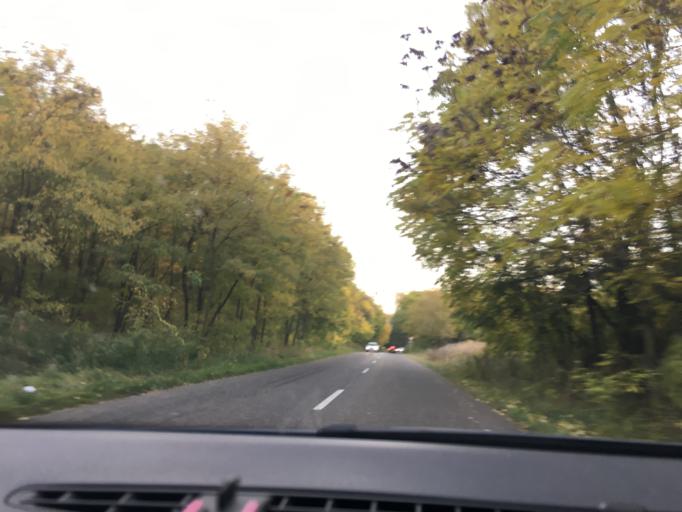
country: HU
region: Szabolcs-Szatmar-Bereg
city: Kisleta
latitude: 47.8522
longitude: 22.0336
